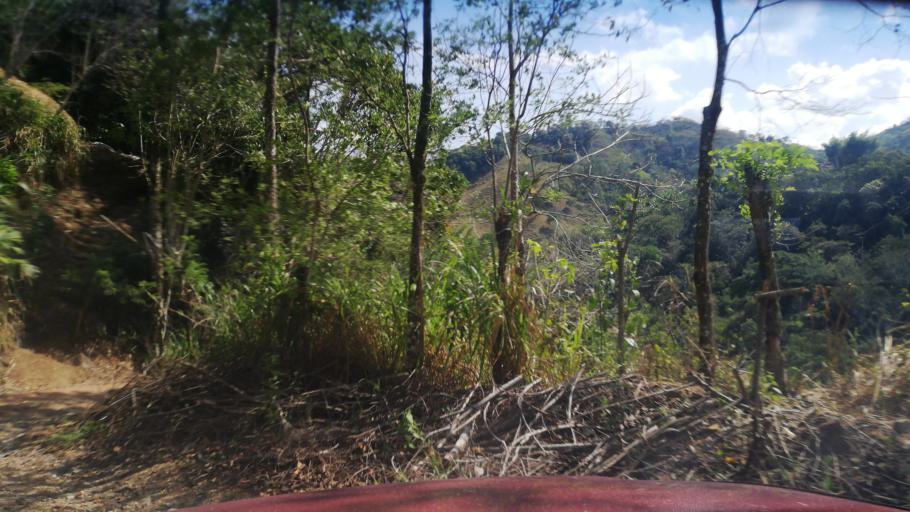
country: CO
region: Risaralda
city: Balboa
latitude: 4.9108
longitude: -75.9519
